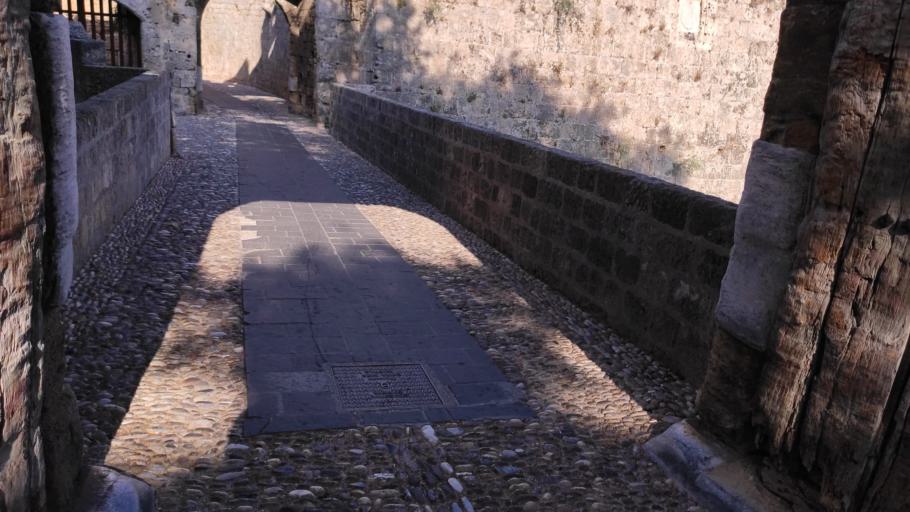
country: GR
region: South Aegean
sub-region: Nomos Dodekanisou
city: Rodos
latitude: 36.4460
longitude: 28.2233
